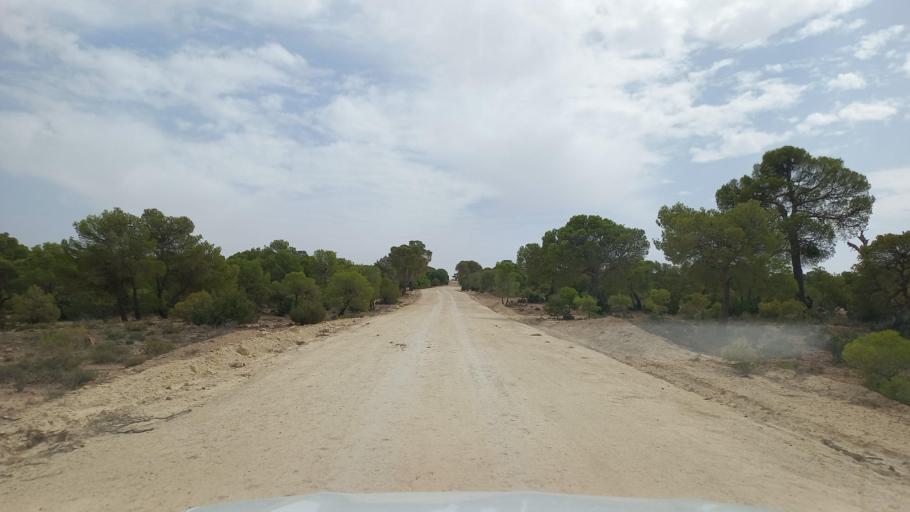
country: TN
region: Al Qasrayn
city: Kasserine
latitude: 35.3811
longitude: 8.8684
